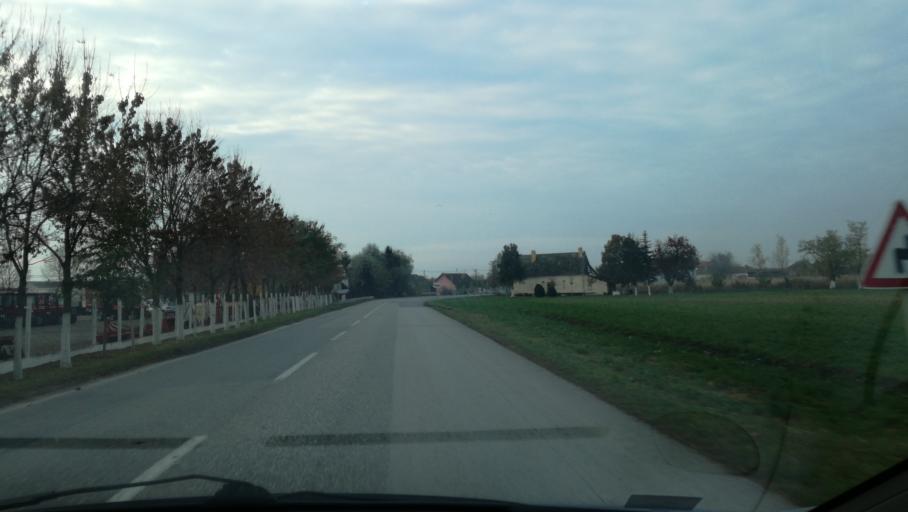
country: RS
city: Basaid
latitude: 45.6497
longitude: 20.4198
